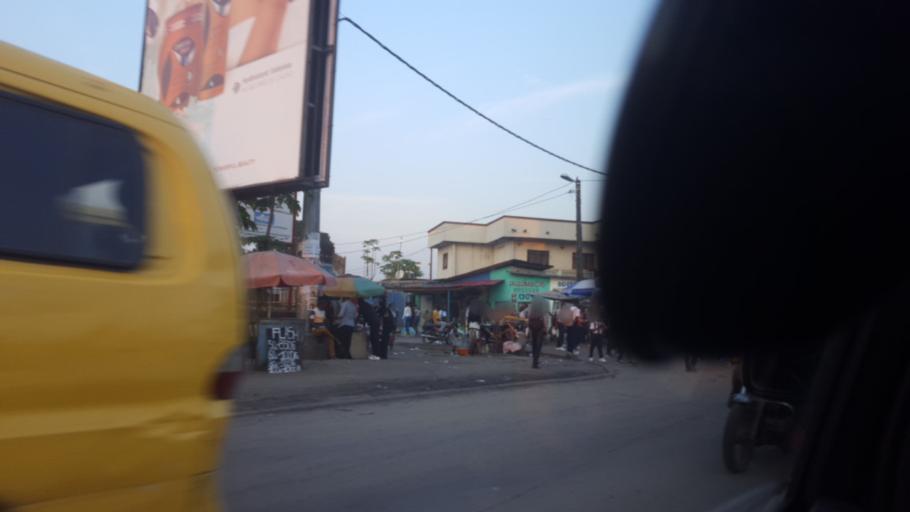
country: CD
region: Kinshasa
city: Kinshasa
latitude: -4.3432
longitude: 15.3213
